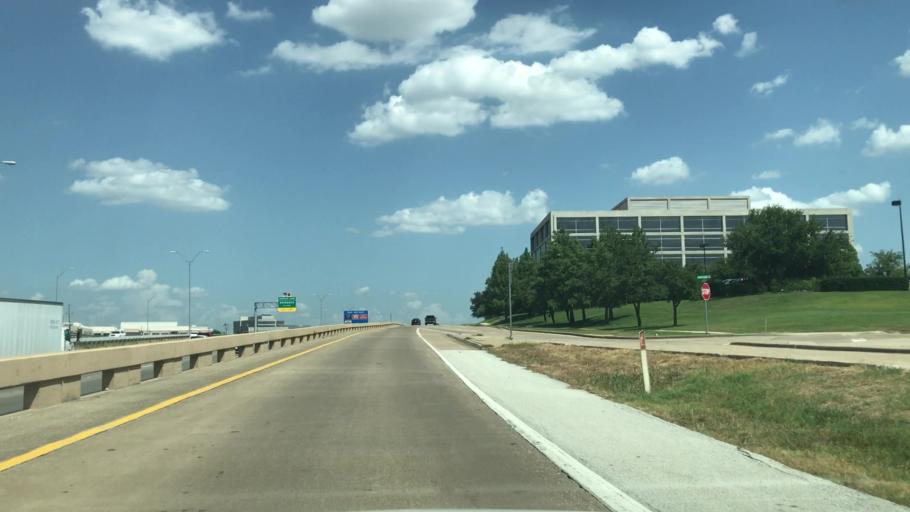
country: US
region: Texas
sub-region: Dallas County
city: Coppell
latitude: 32.9013
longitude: -96.9835
